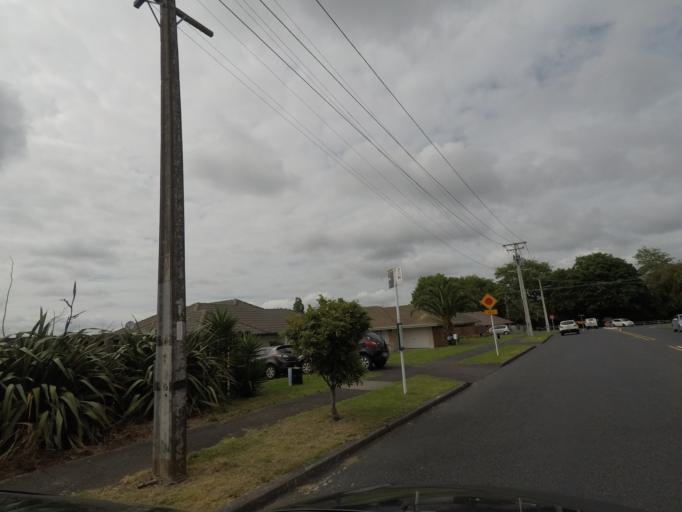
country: NZ
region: Auckland
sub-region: Auckland
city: Waitakere
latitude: -36.9027
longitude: 174.6214
